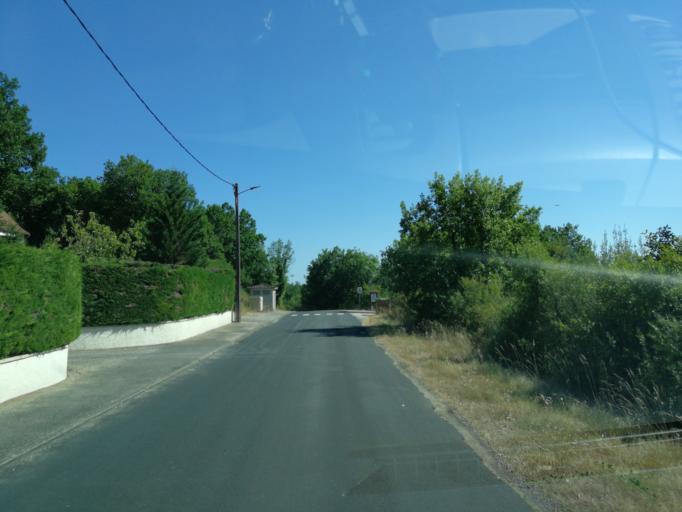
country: FR
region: Midi-Pyrenees
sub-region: Departement du Lot
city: Souillac
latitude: 44.9112
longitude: 1.4822
